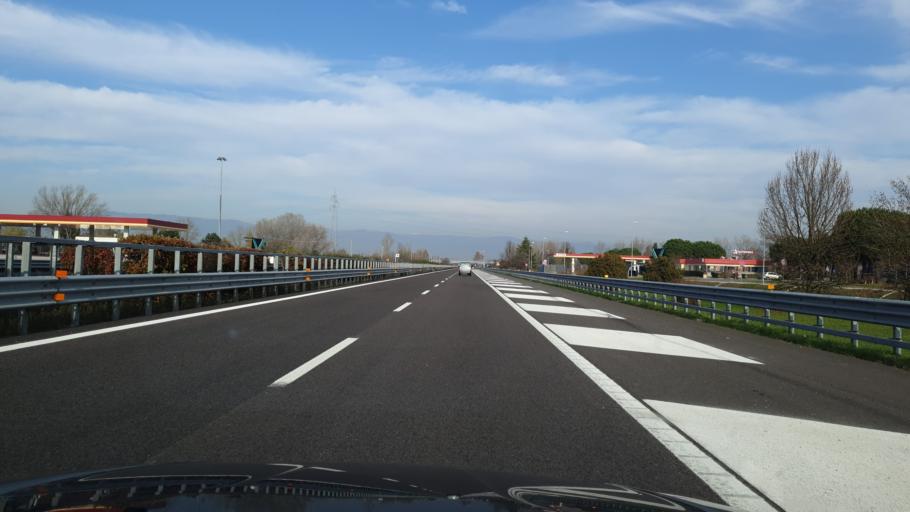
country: IT
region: Veneto
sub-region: Provincia di Vicenza
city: Vigardolo
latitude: 45.5929
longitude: 11.5991
